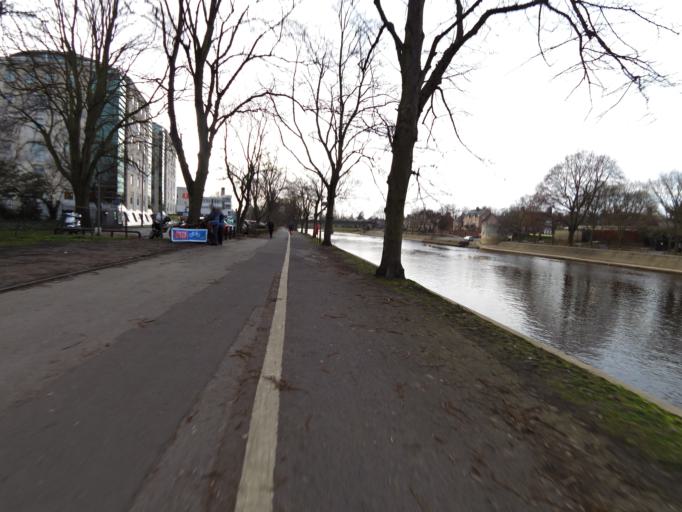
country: GB
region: England
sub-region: City of York
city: York
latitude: 53.9603
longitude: -1.0896
